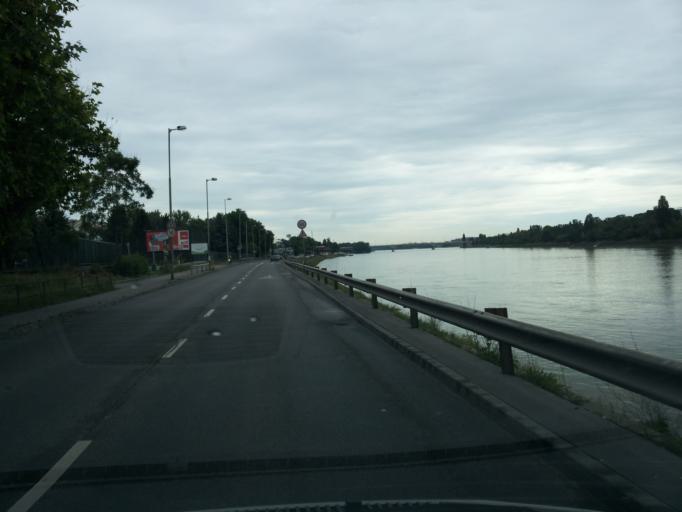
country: HU
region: Budapest
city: Budapest III. keruelet
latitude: 47.5267
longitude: 19.0406
